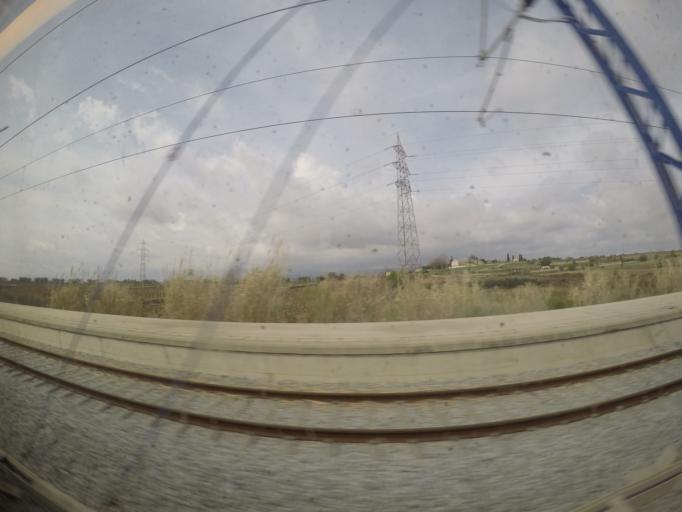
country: ES
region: Catalonia
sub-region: Provincia de Tarragona
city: Santa Oliva
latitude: 41.2519
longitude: 1.5742
